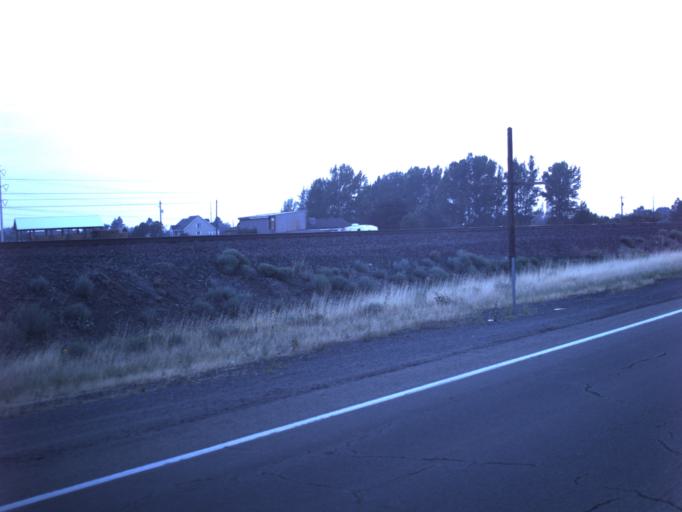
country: US
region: Utah
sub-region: Utah County
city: Mapleton
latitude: 40.0997
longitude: -111.5952
